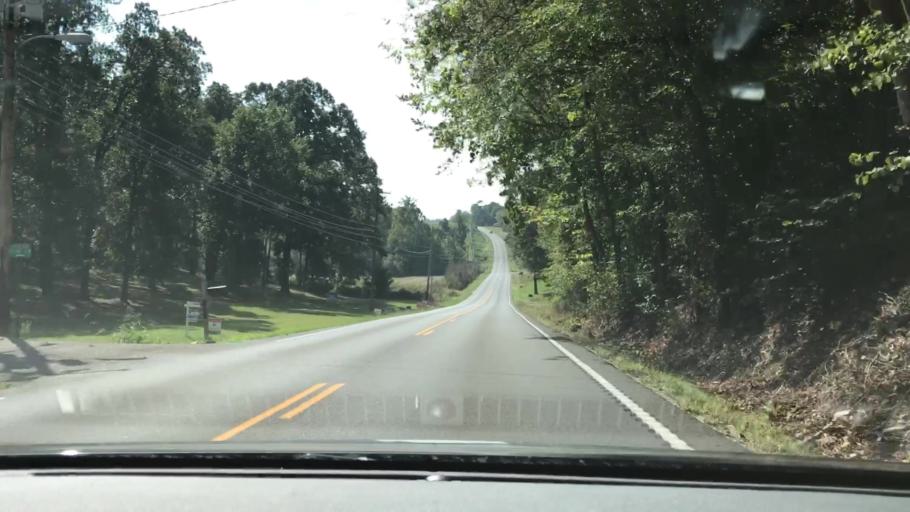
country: US
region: Kentucky
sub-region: Marshall County
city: Benton
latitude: 36.8271
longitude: -88.3505
